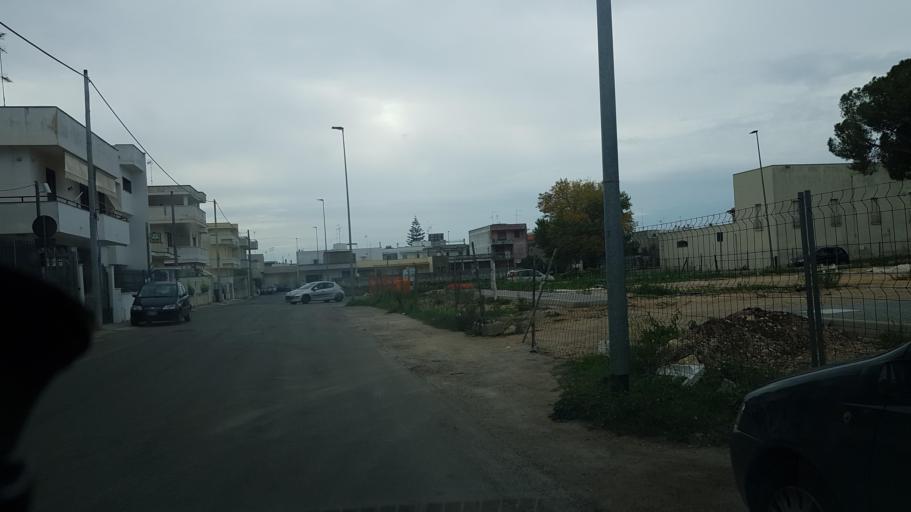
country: IT
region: Apulia
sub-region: Provincia di Lecce
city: Leverano
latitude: 40.2889
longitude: 17.9937
